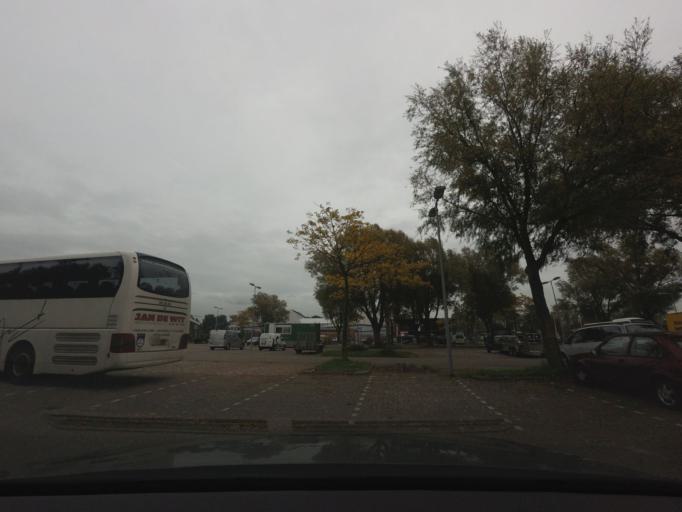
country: NL
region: North Holland
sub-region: Gemeente Alkmaar
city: Alkmaar
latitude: 52.6351
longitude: 4.7141
